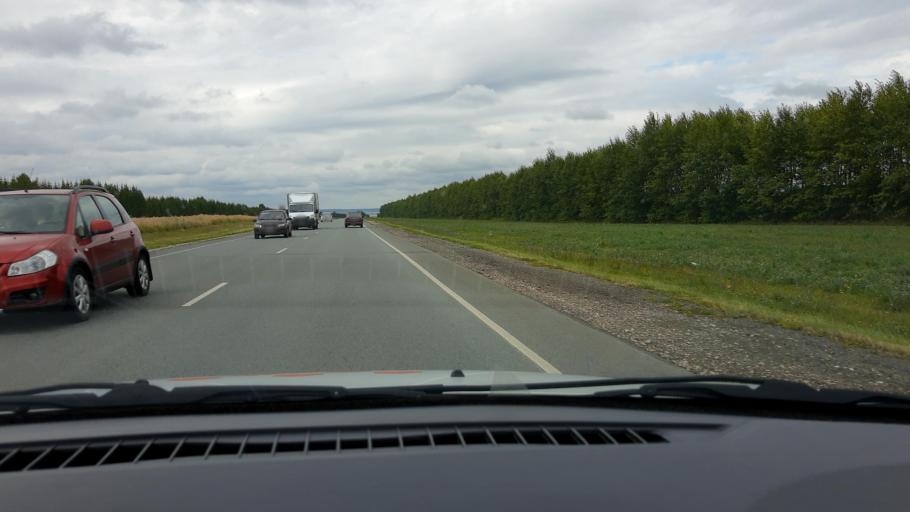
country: RU
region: Tatarstan
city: Laishevo
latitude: 55.3932
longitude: 49.7862
